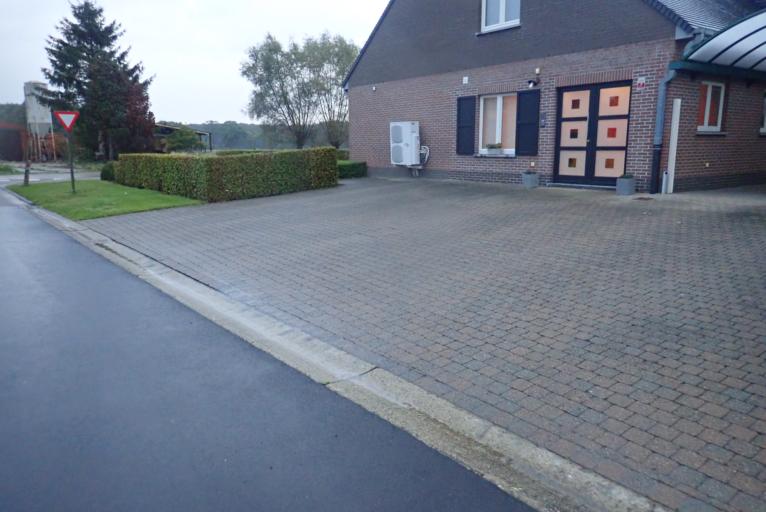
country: BE
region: Flanders
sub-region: Provincie Antwerpen
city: Hulshout
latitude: 51.0570
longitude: 4.7692
